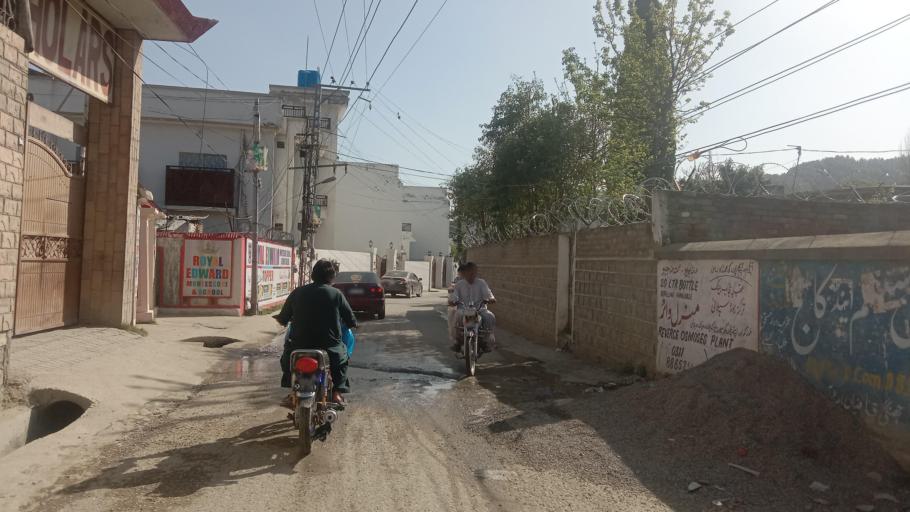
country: PK
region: Khyber Pakhtunkhwa
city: Abbottabad
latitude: 34.1727
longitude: 73.2238
